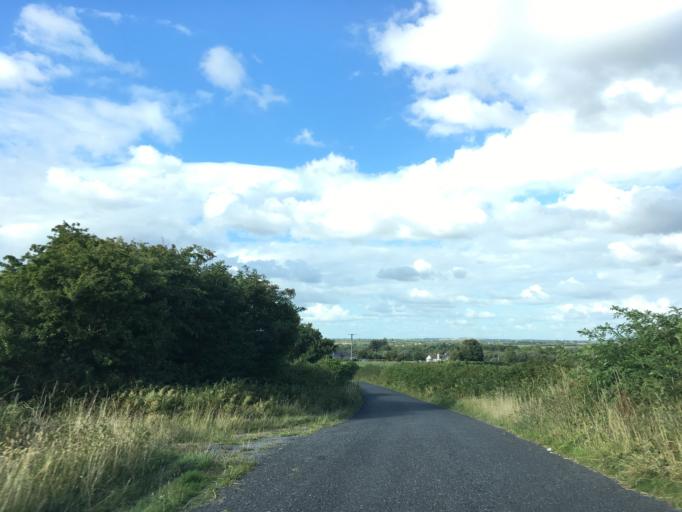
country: IE
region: Munster
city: Cahir
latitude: 52.2682
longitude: -7.9577
